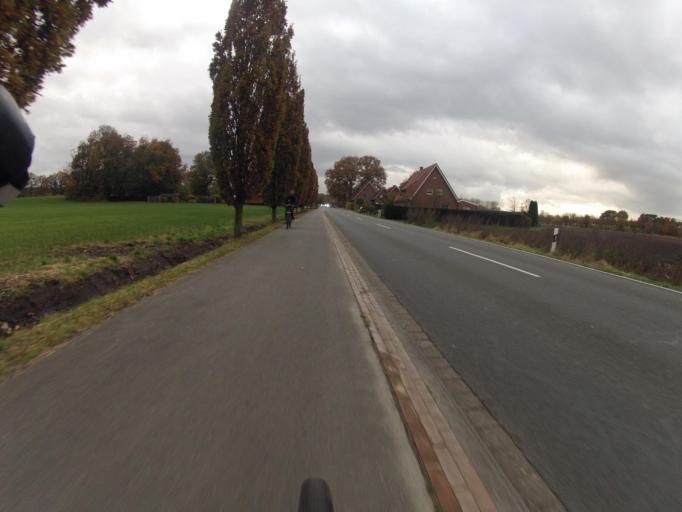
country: DE
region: North Rhine-Westphalia
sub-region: Regierungsbezirk Munster
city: Horstel
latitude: 52.2862
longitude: 7.6112
